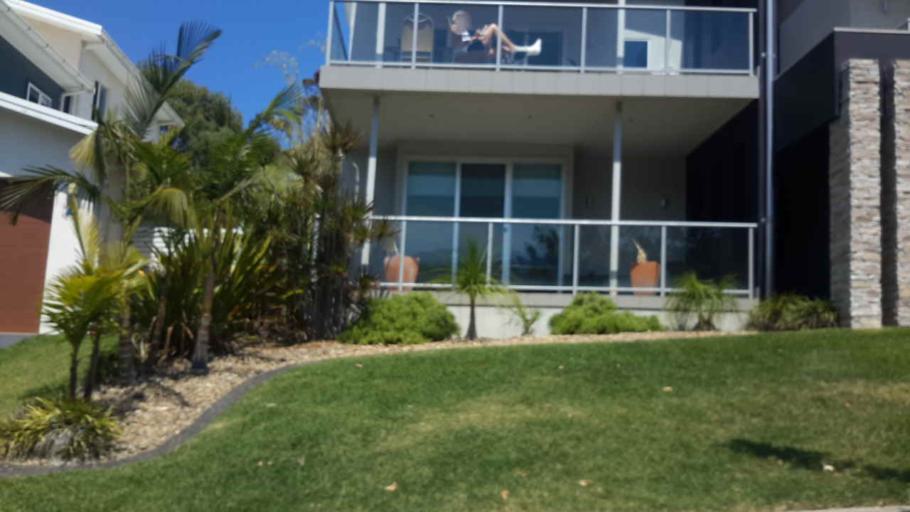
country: AU
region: New South Wales
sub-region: Wollongong
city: Bulli
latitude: -34.3286
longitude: 150.9181
